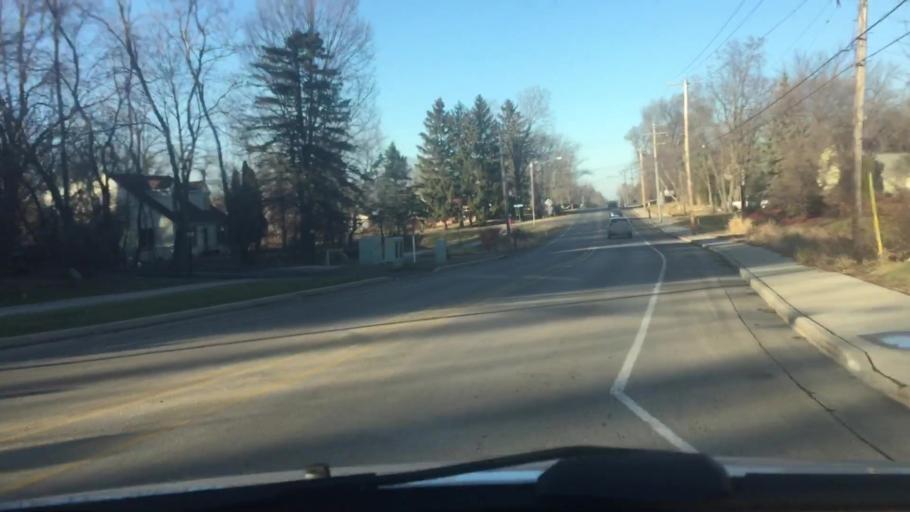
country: US
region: Wisconsin
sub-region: Waukesha County
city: Brookfield
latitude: 43.0616
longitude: -88.1459
